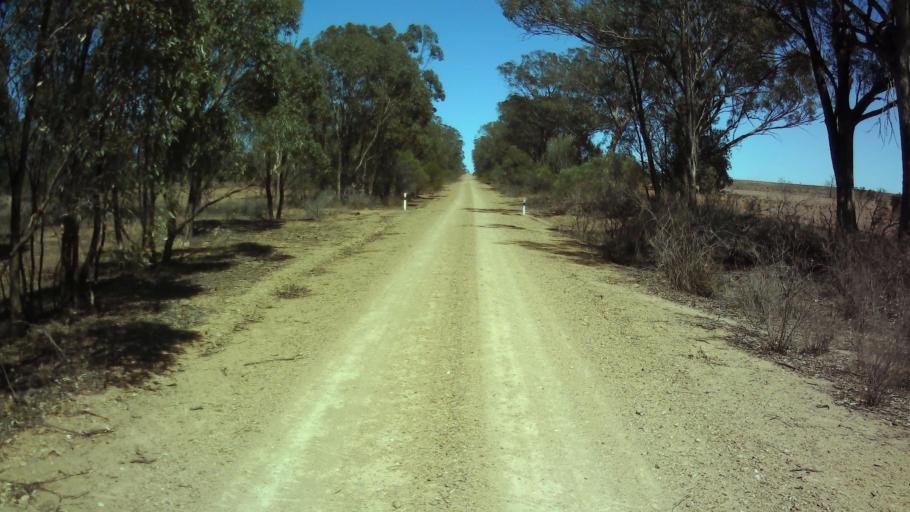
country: AU
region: New South Wales
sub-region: Forbes
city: Forbes
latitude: -33.6961
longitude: 147.8433
